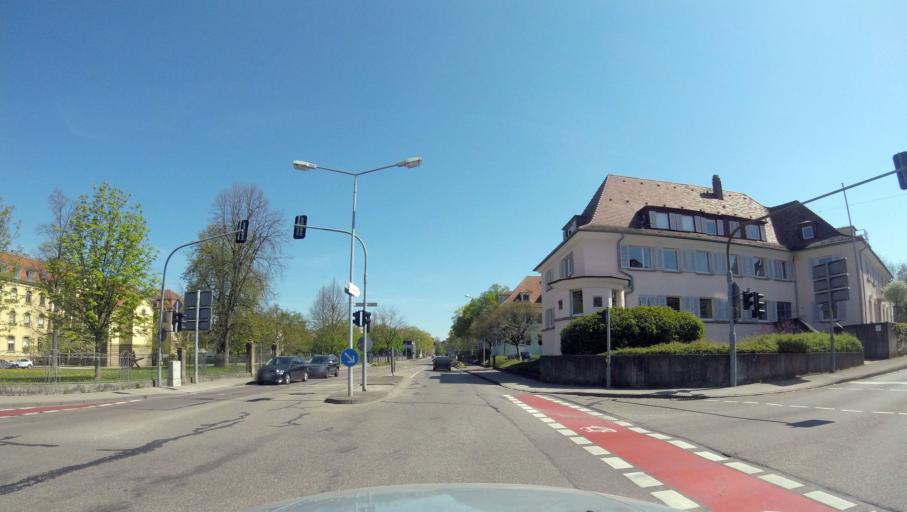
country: DE
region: Baden-Wuerttemberg
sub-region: Regierungsbezirk Stuttgart
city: Schwabisch Gmund
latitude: 48.7950
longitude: 9.7907
